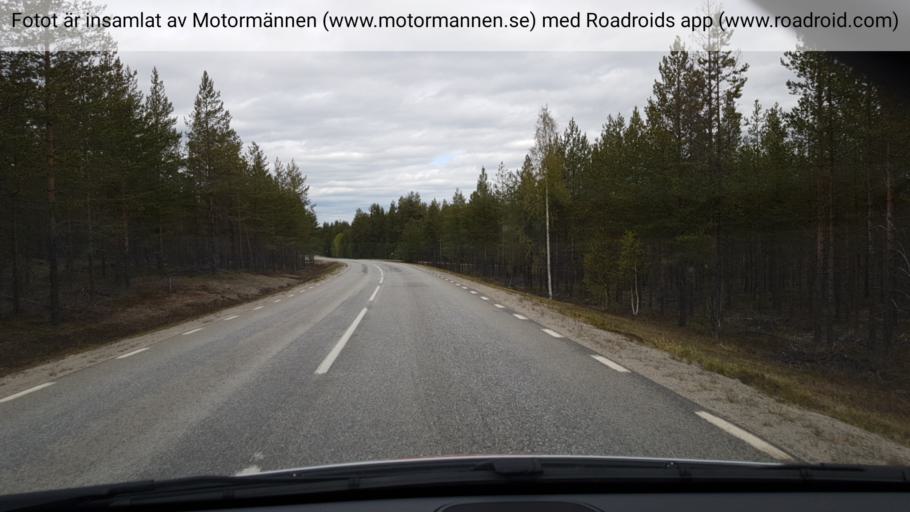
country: SE
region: Vaesterbotten
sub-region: Mala Kommun
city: Mala
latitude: 64.8878
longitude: 18.7296
